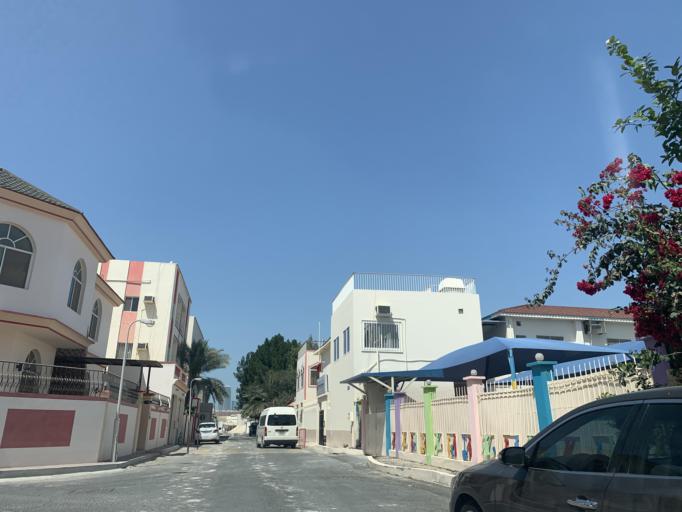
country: BH
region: Manama
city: Manama
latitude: 26.2099
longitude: 50.5737
